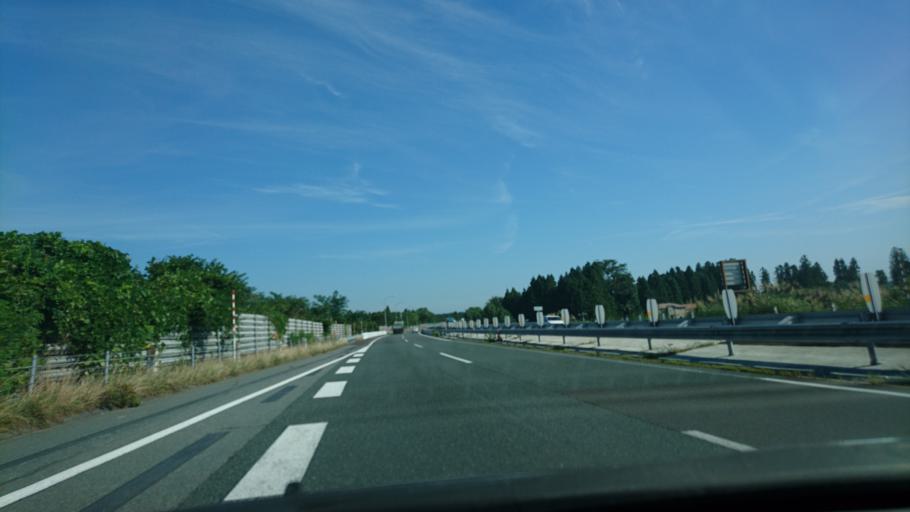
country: JP
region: Iwate
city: Mizusawa
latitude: 39.0732
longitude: 141.0998
